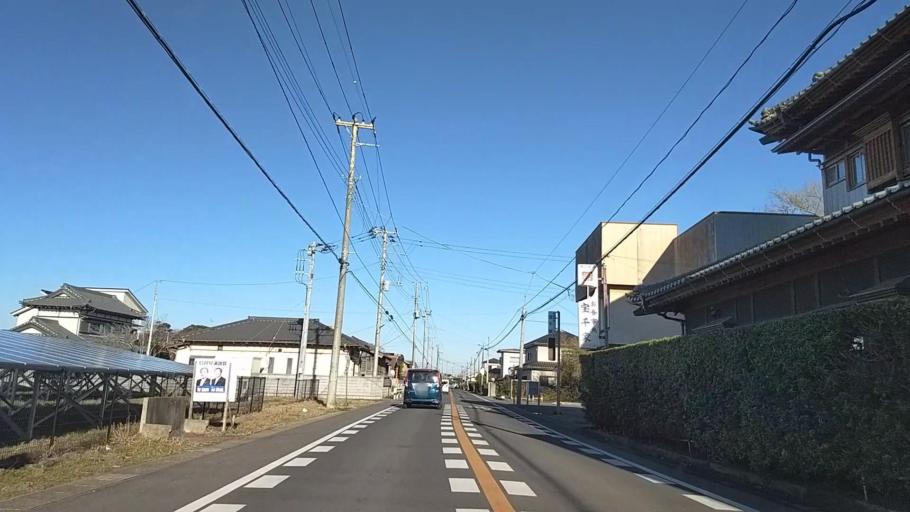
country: JP
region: Chiba
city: Yokaichiba
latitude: 35.6437
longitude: 140.5751
